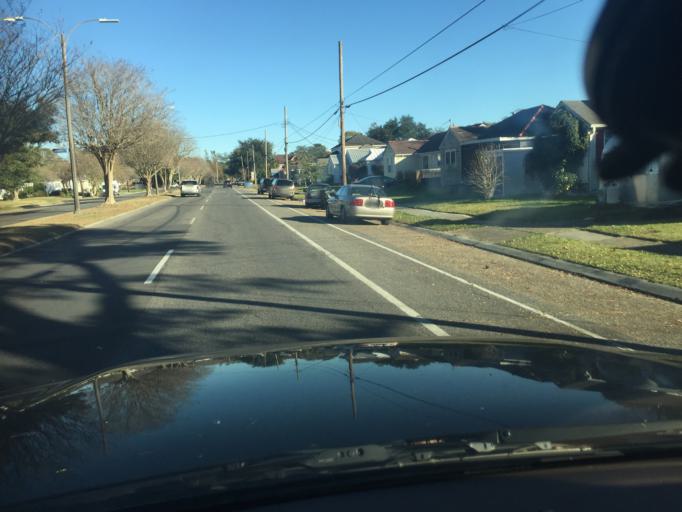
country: US
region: Louisiana
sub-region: Orleans Parish
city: New Orleans
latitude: 29.9887
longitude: -90.0781
